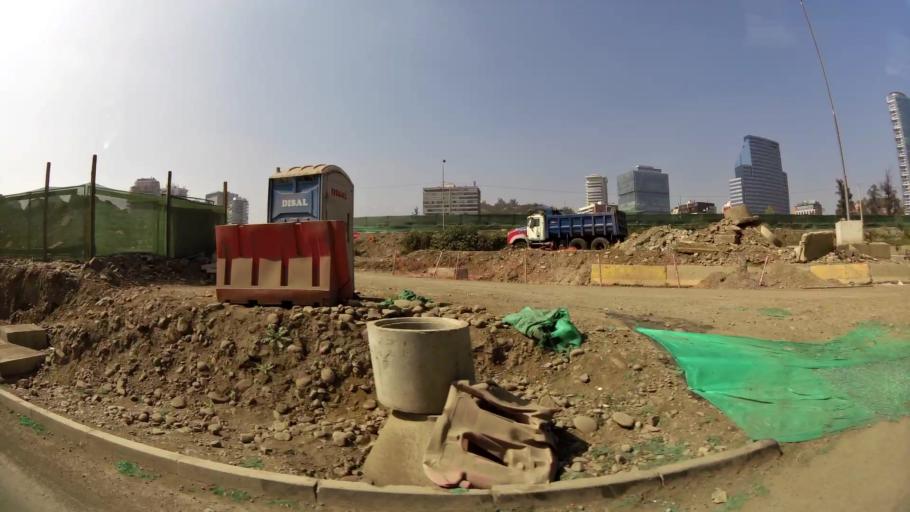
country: CL
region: Santiago Metropolitan
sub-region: Provincia de Santiago
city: Villa Presidente Frei, Nunoa, Santiago, Chile
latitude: -33.4078
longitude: -70.6040
